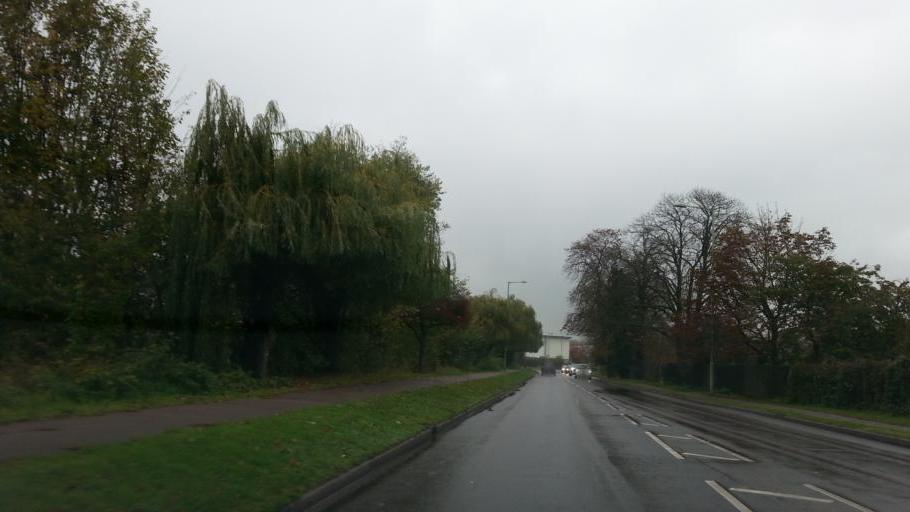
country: GB
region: England
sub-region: Suffolk
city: Haverhill
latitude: 52.0792
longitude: 0.4462
